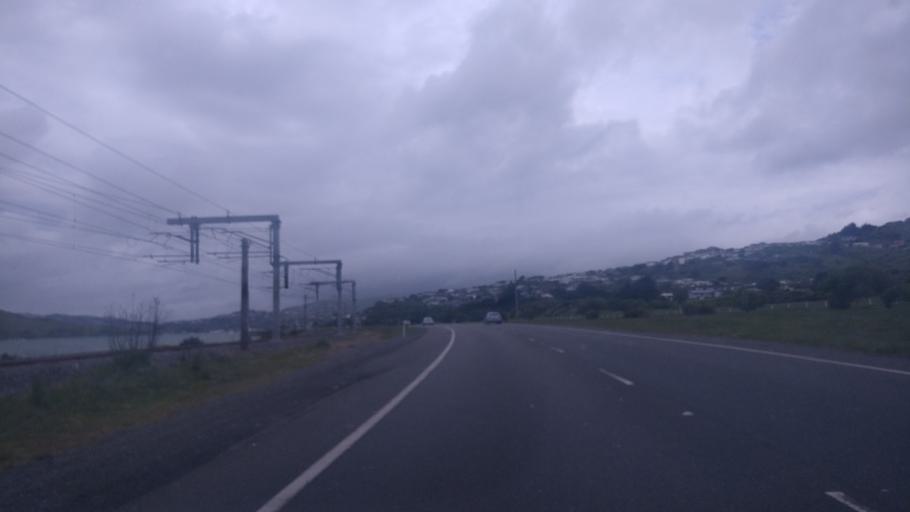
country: NZ
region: Wellington
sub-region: Porirua City
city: Porirua
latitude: -41.1164
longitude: 174.8582
